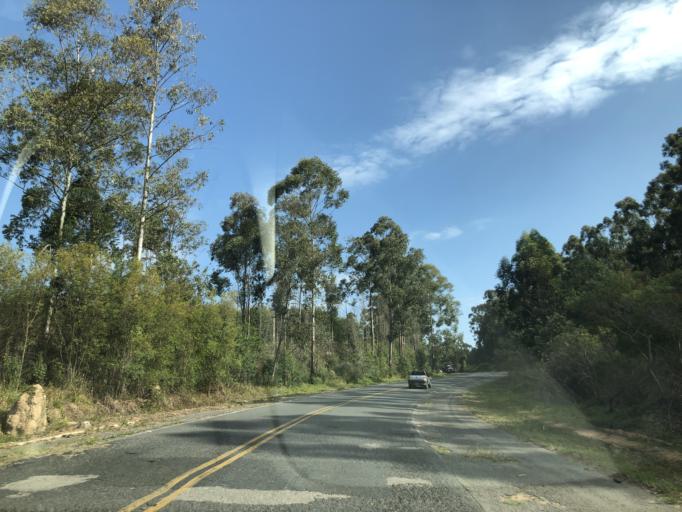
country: BR
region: Sao Paulo
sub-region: Pilar Do Sul
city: Pilar do Sul
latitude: -23.8147
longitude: -47.6467
